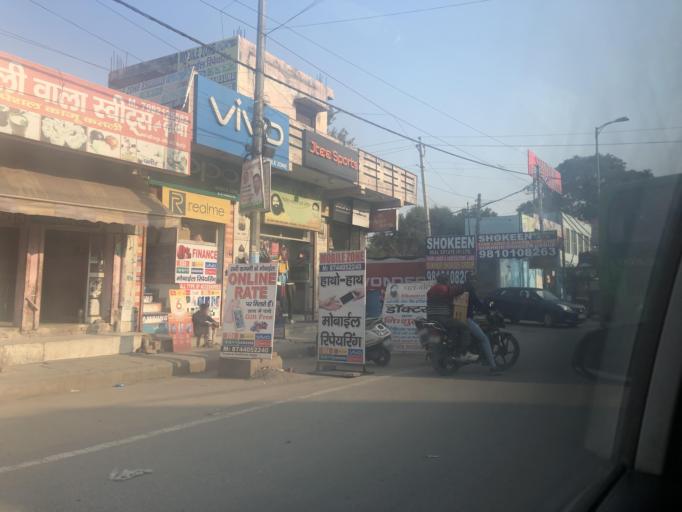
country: IN
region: Haryana
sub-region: Gurgaon
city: Gurgaon
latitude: 28.5583
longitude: 77.0041
